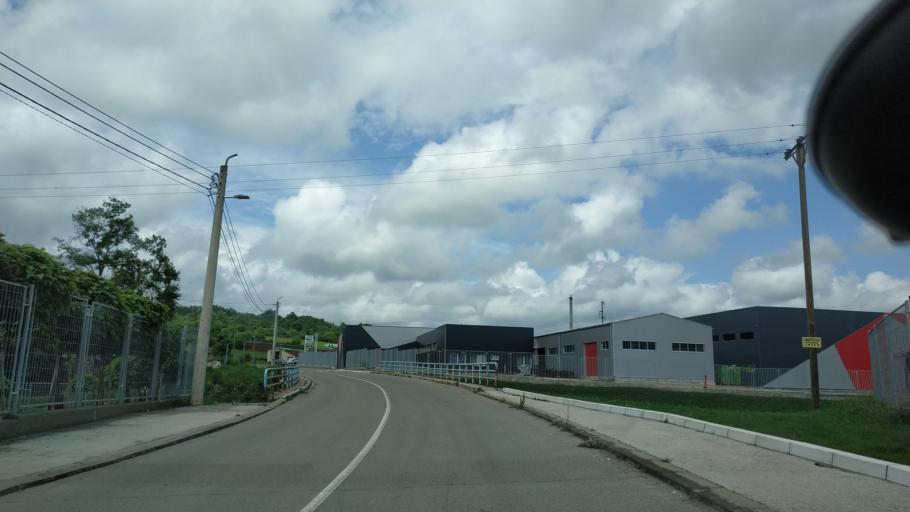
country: RS
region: Central Serbia
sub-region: Zajecarski Okrug
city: Boljevac
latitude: 43.8342
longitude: 21.9585
